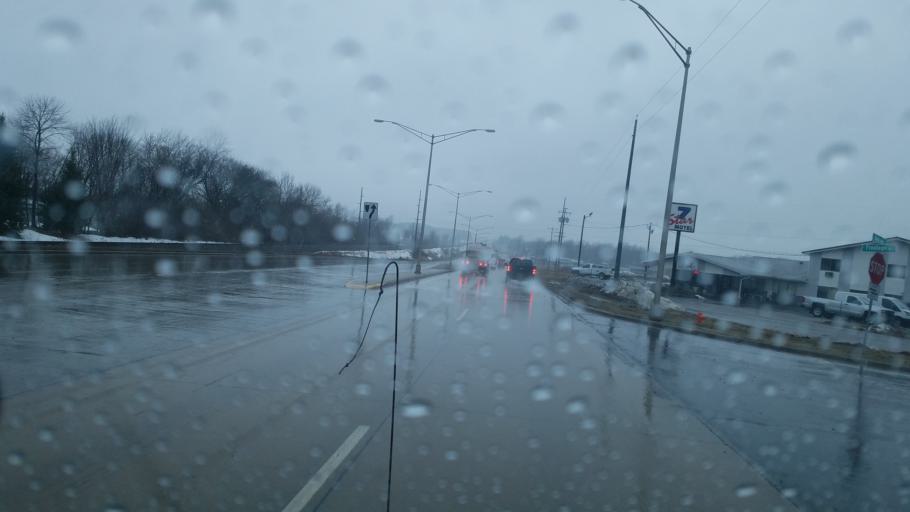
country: US
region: Wisconsin
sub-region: Wood County
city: Marshfield
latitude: 44.6838
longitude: -90.1947
